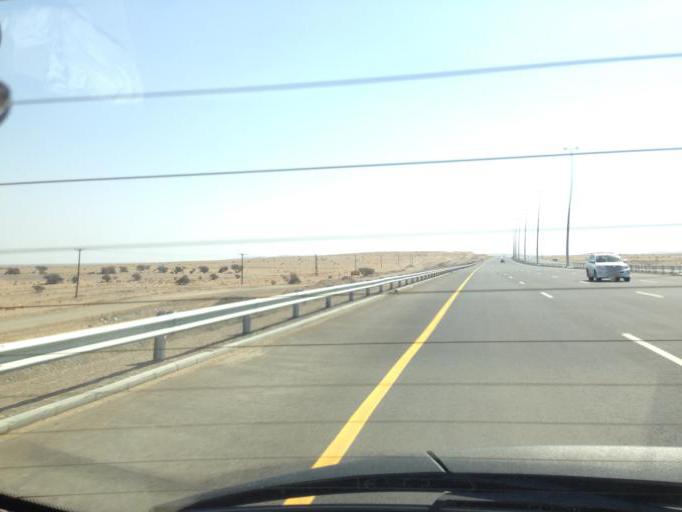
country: OM
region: Al Batinah
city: Rustaq
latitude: 23.5322
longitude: 57.5824
